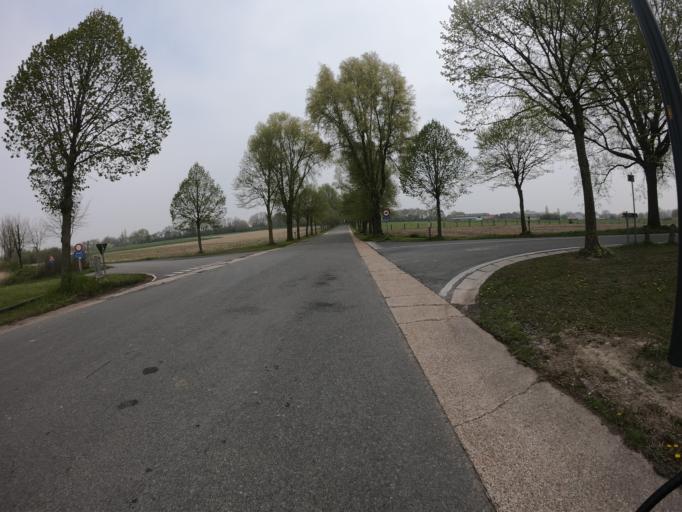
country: BE
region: Flanders
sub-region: Provincie West-Vlaanderen
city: Zwevegem
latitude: 50.7792
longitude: 3.3809
